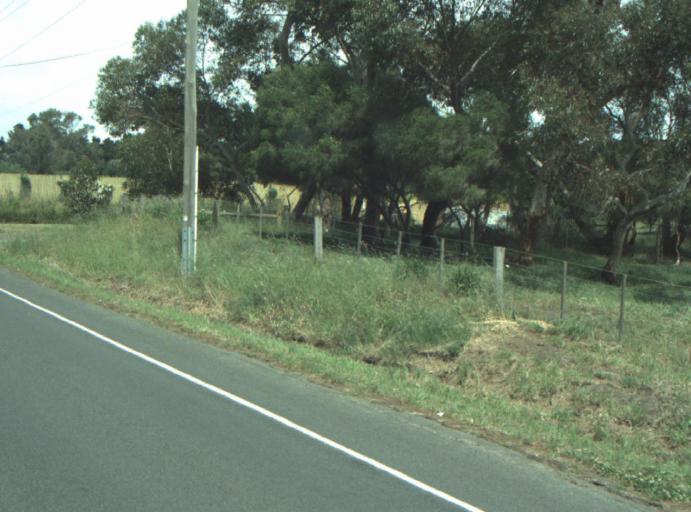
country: AU
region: Victoria
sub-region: Greater Geelong
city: Clifton Springs
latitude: -38.1491
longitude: 144.5944
